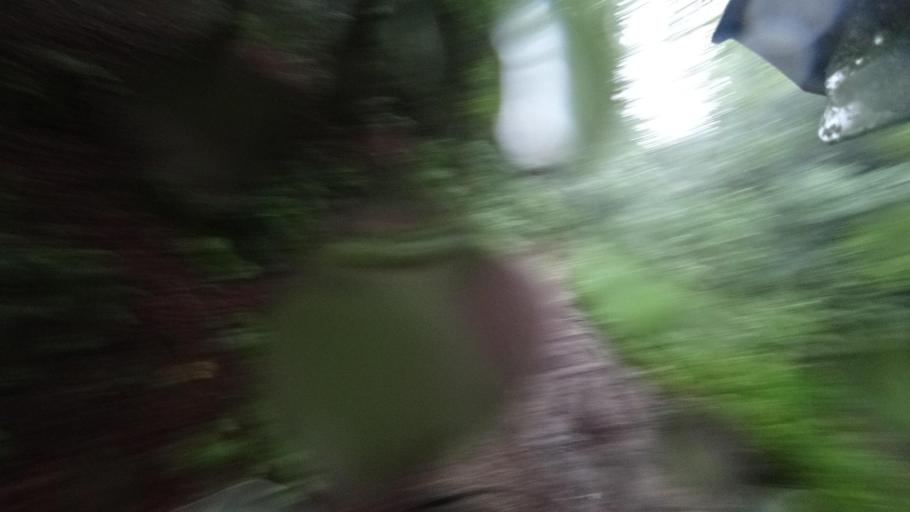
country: HR
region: Licko-Senjska
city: Jezerce
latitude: 44.8269
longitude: 15.6162
